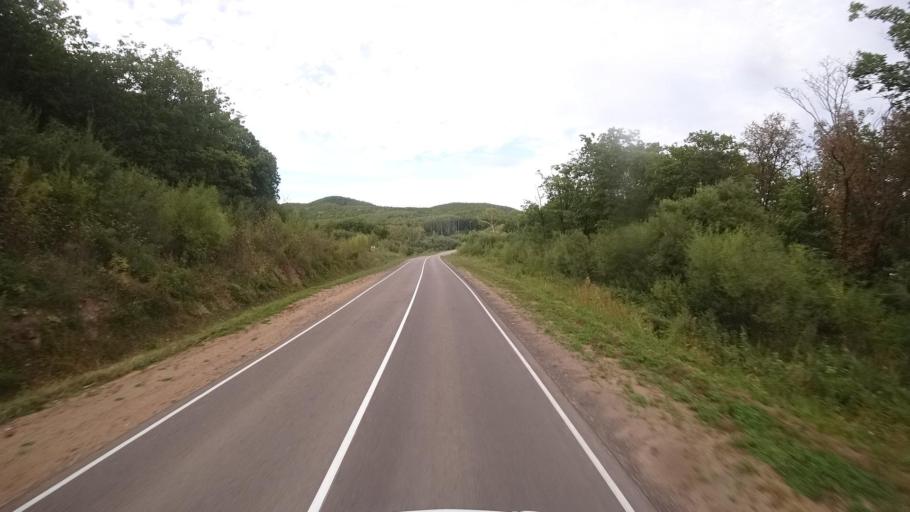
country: RU
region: Primorskiy
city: Yakovlevka
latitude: 44.3820
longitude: 133.4572
